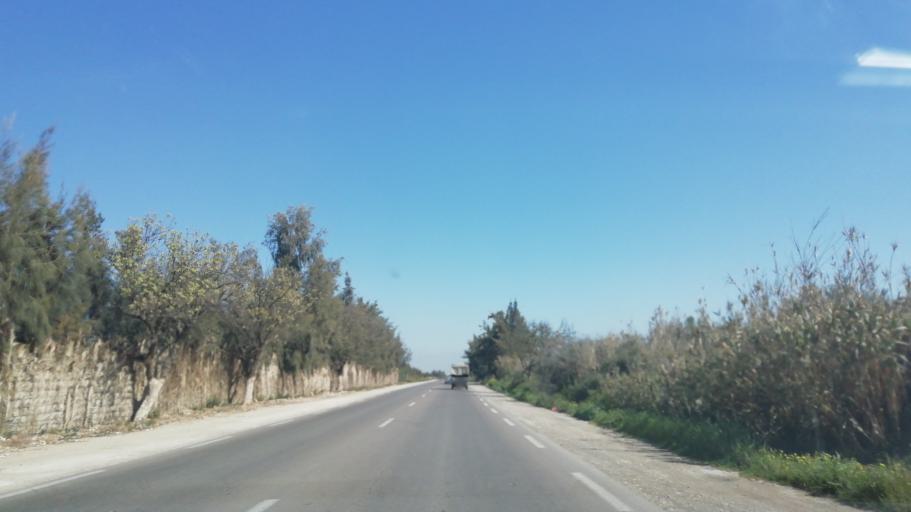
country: DZ
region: Mascara
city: Sig
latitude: 35.5483
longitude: -0.1172
